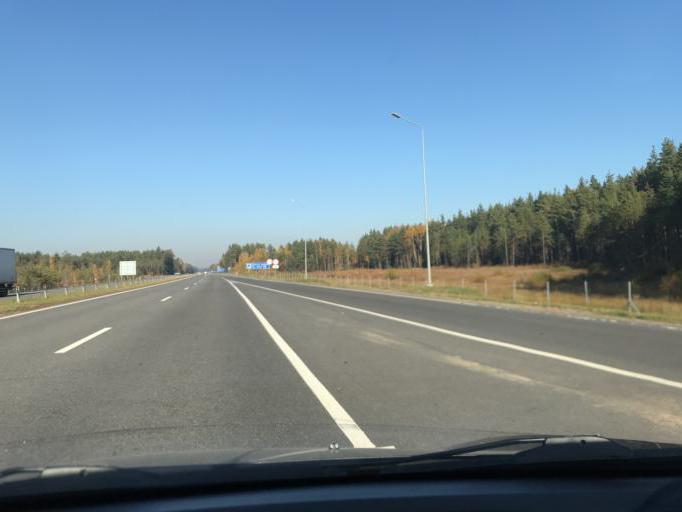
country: BY
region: Mogilev
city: Babruysk
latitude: 53.1924
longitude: 29.3533
